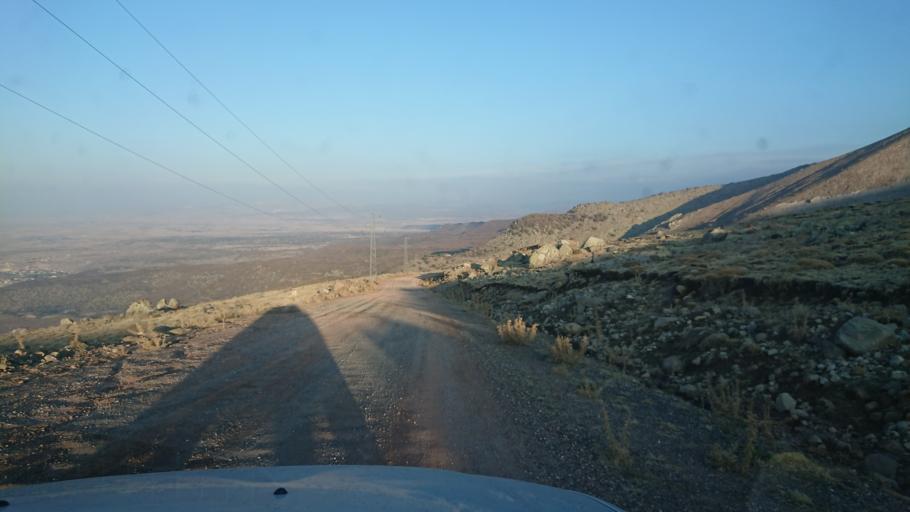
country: TR
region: Aksaray
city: Taspinar
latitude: 38.1608
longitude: 34.1717
